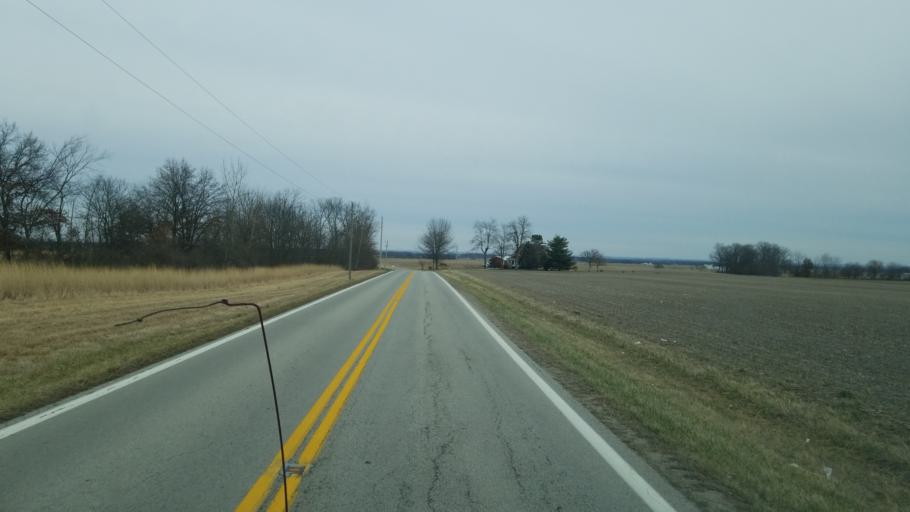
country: US
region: Ohio
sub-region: Ross County
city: Frankfort
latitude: 39.4856
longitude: -83.1799
